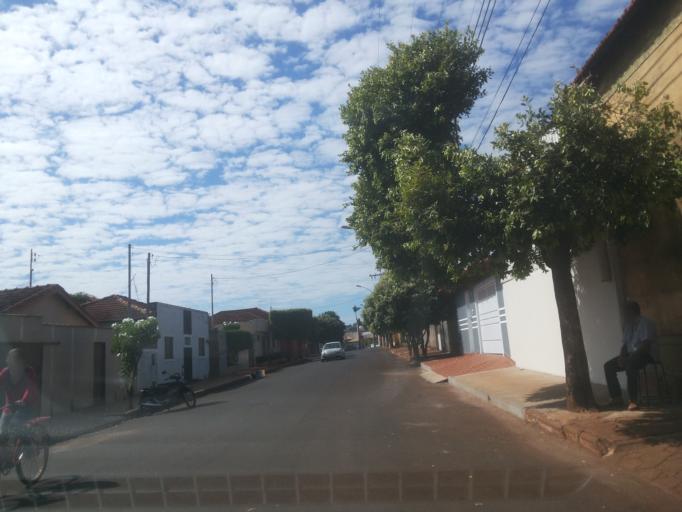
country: BR
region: Minas Gerais
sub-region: Centralina
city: Centralina
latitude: -18.5879
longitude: -49.2000
